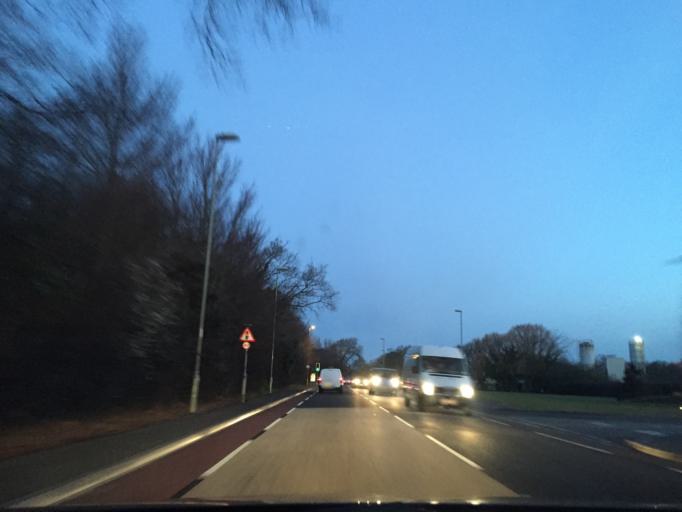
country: GB
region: England
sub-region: Hampshire
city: Fareham
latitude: 50.8303
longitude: -1.1694
